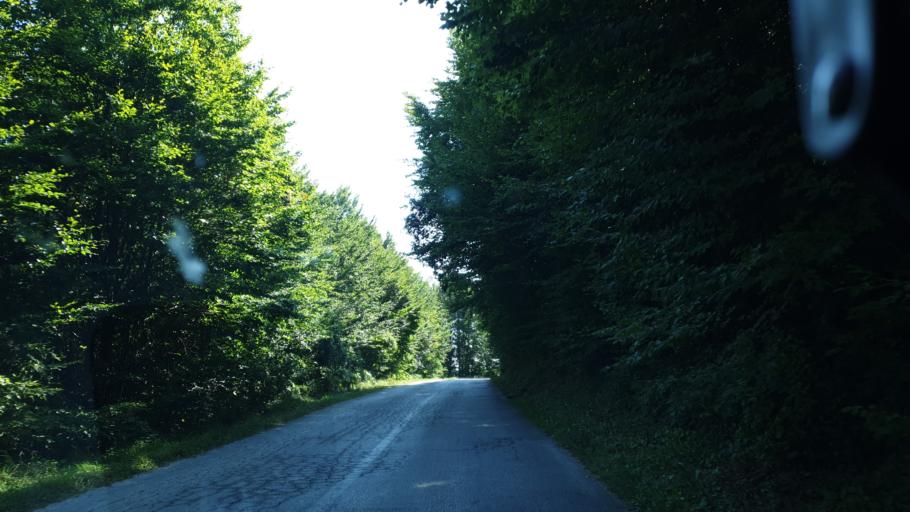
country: RS
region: Central Serbia
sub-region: Zlatiborski Okrug
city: Cajetina
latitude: 43.7063
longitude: 19.8424
